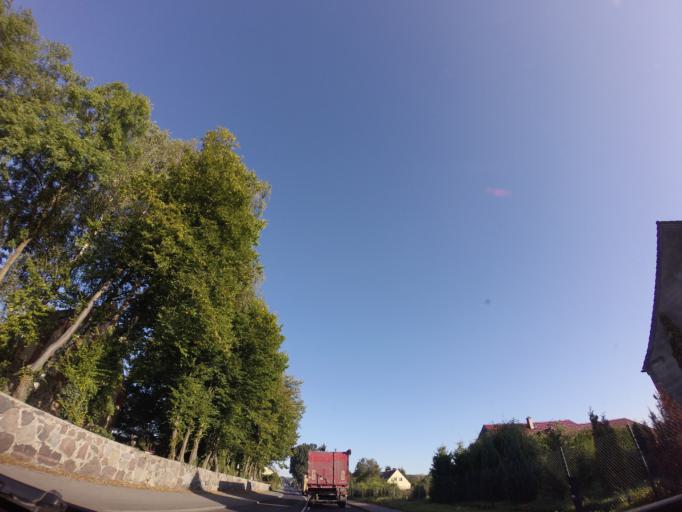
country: PL
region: West Pomeranian Voivodeship
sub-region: Powiat goleniowski
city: Maszewo
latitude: 53.4490
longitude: 15.0645
